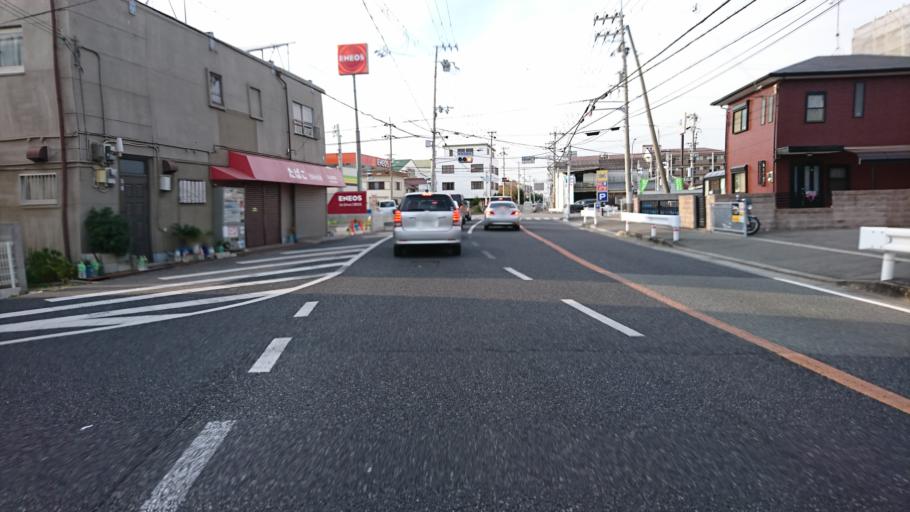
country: JP
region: Hyogo
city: Kakogawacho-honmachi
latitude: 34.7029
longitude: 134.8749
